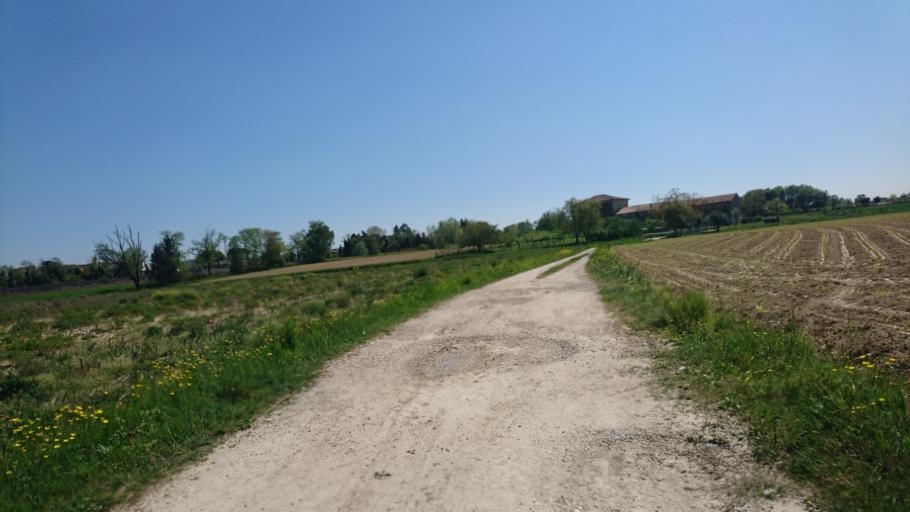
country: IT
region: Veneto
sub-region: Provincia di Treviso
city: Casier
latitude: 45.6367
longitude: 12.2744
